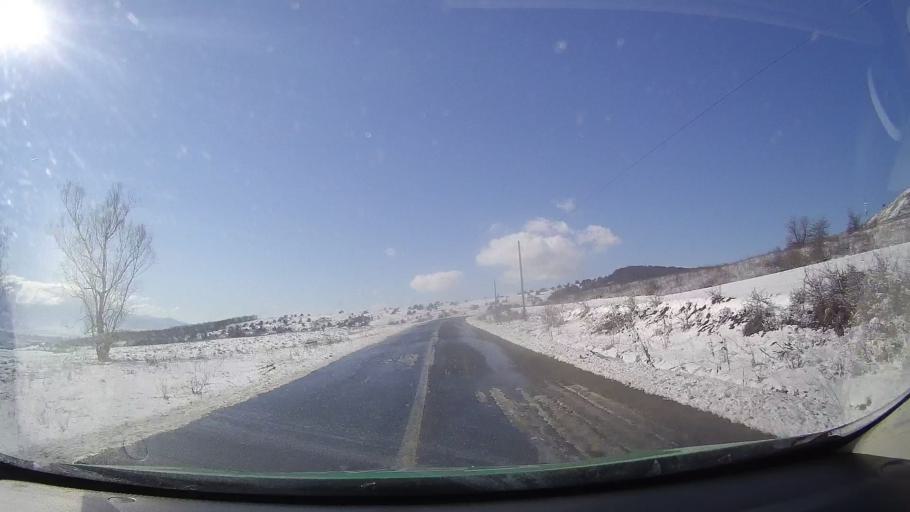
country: RO
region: Sibiu
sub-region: Comuna Avrig
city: Avrig
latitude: 45.7724
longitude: 24.3750
